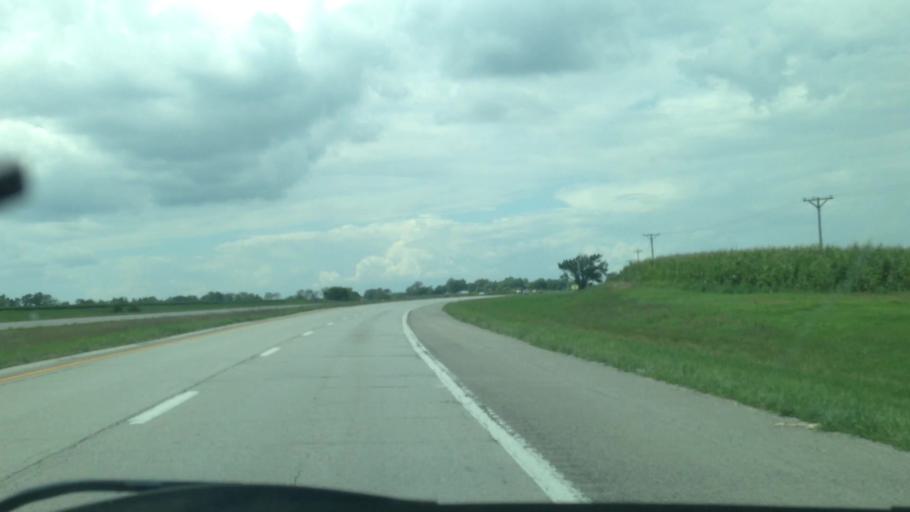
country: US
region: Missouri
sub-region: Pike County
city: Bowling Green
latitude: 39.2761
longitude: -91.0929
